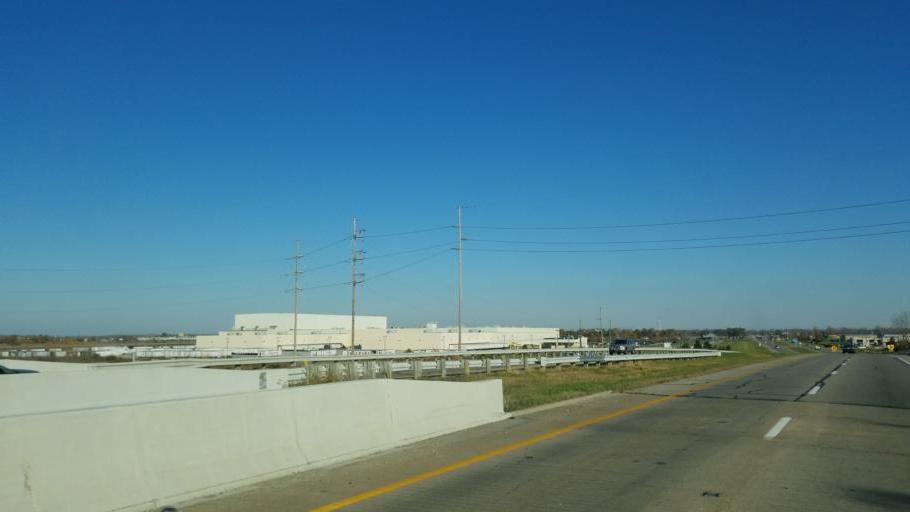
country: US
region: Ohio
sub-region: Wood County
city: Rossford
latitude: 41.5640
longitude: -83.5511
